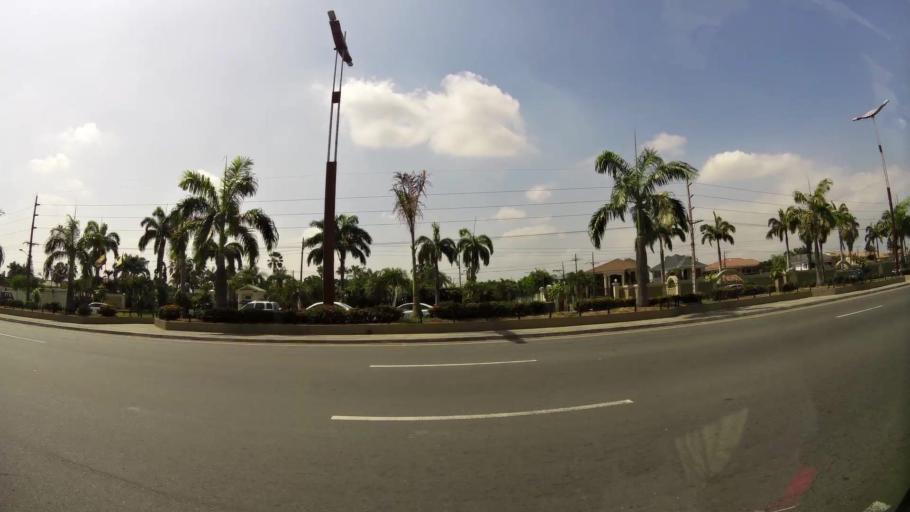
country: EC
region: Guayas
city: Eloy Alfaro
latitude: -2.1310
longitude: -79.8632
